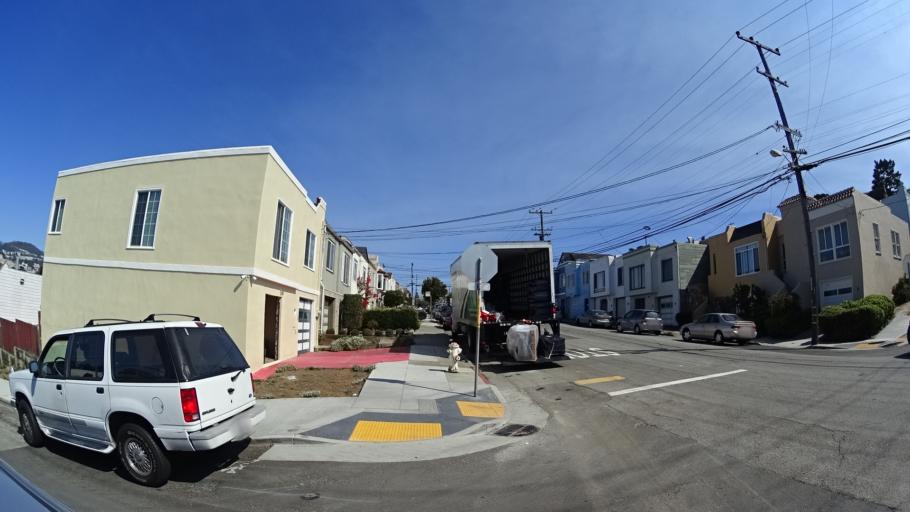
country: US
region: California
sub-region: San Mateo County
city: Daly City
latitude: 37.7198
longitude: -122.4681
